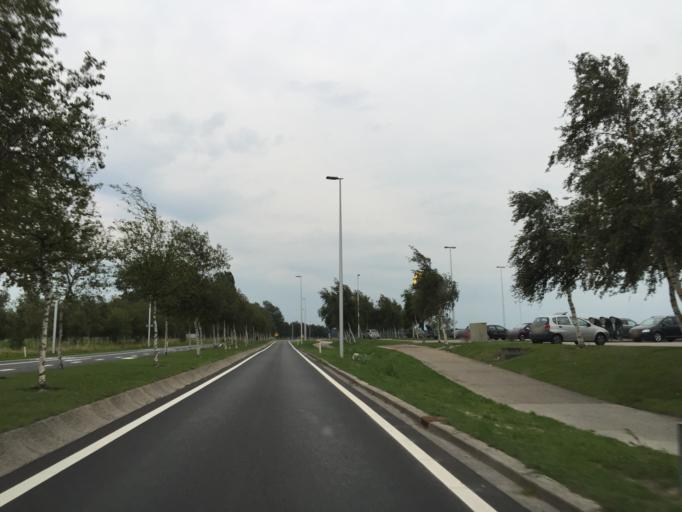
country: NL
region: North Holland
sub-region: Gemeente Aalsmeer
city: Aalsmeer
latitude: 52.3214
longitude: 4.7930
